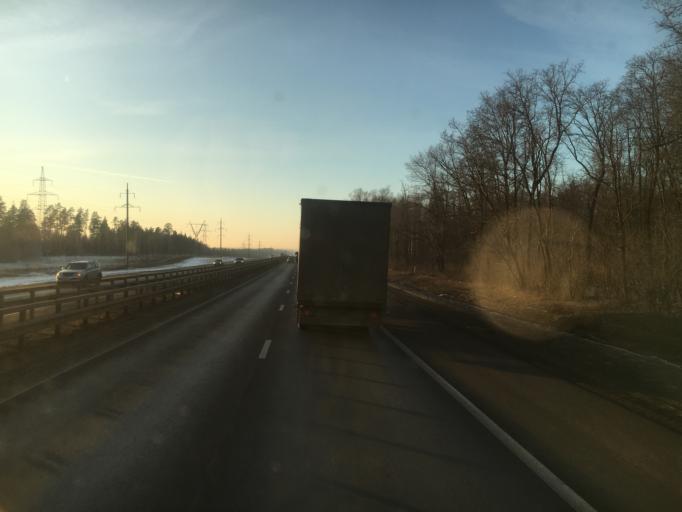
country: RU
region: Samara
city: Povolzhskiy
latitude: 53.5181
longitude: 49.7921
